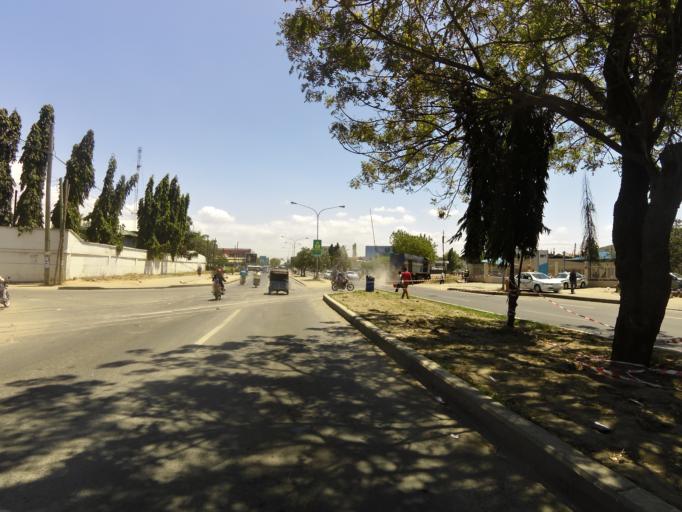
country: TZ
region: Dar es Salaam
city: Dar es Salaam
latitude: -6.8269
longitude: 39.2774
